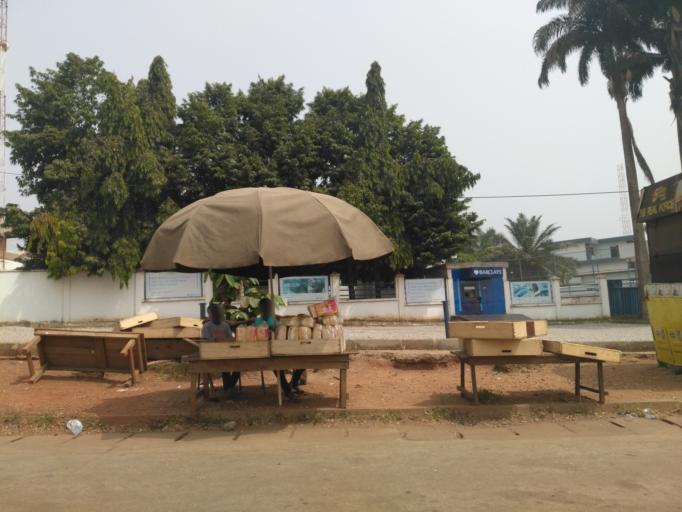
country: GH
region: Ashanti
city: Kumasi
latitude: 6.6736
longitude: -1.6423
